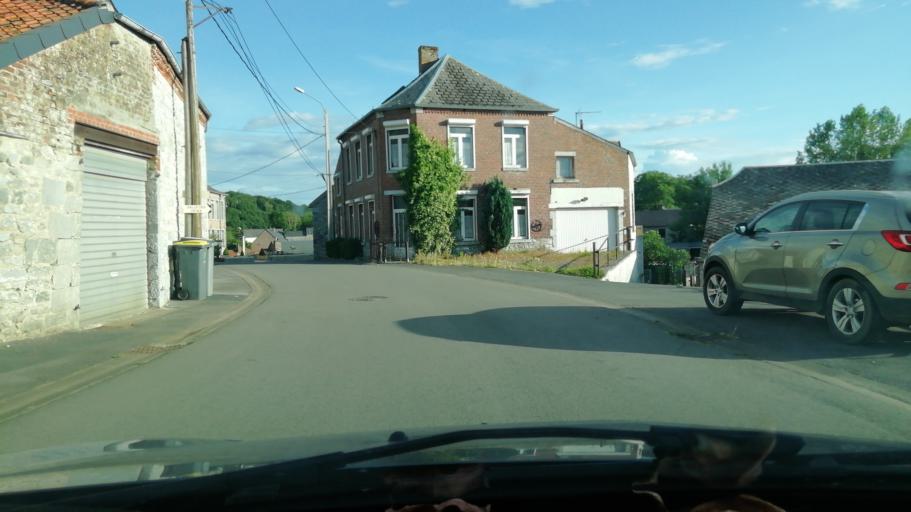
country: BE
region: Wallonia
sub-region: Province du Hainaut
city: Merbes-le-Chateau
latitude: 50.2634
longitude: 4.1816
